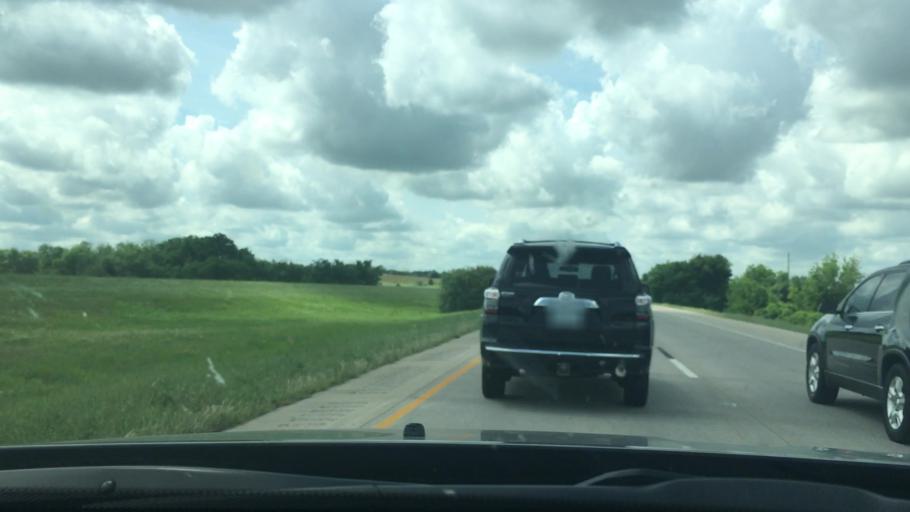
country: US
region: Oklahoma
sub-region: Love County
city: Marietta
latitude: 33.8668
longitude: -97.1343
